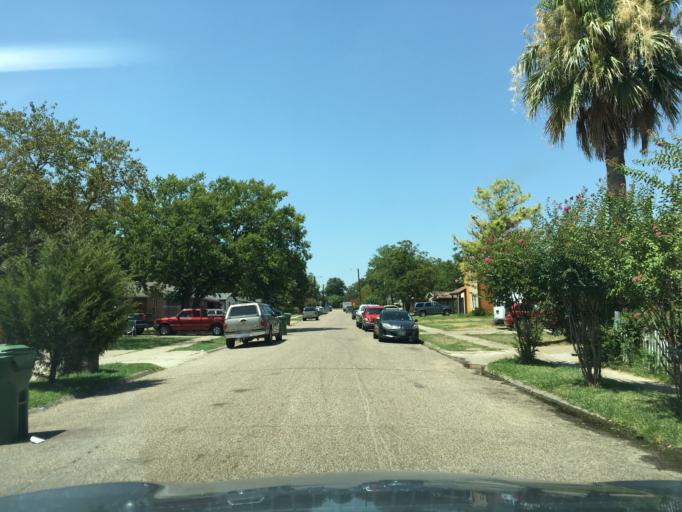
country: US
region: Texas
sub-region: Dallas County
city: Garland
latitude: 32.8969
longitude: -96.6268
